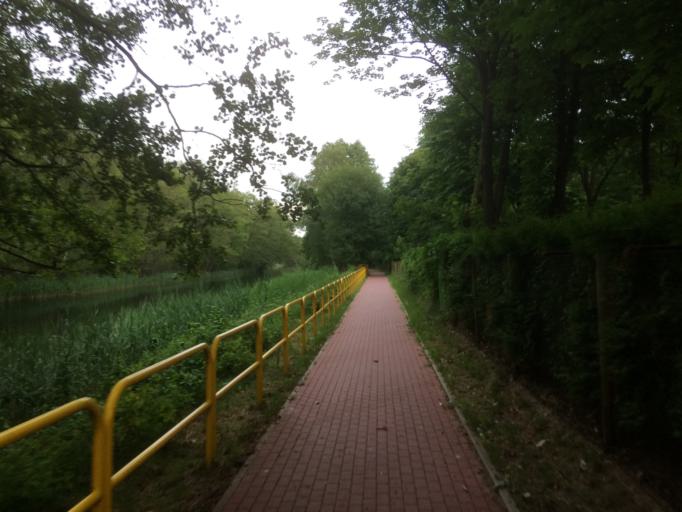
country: PL
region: Lubusz
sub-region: Powiat swiebodzinski
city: Miedzylesie
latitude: 52.2134
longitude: 15.4137
